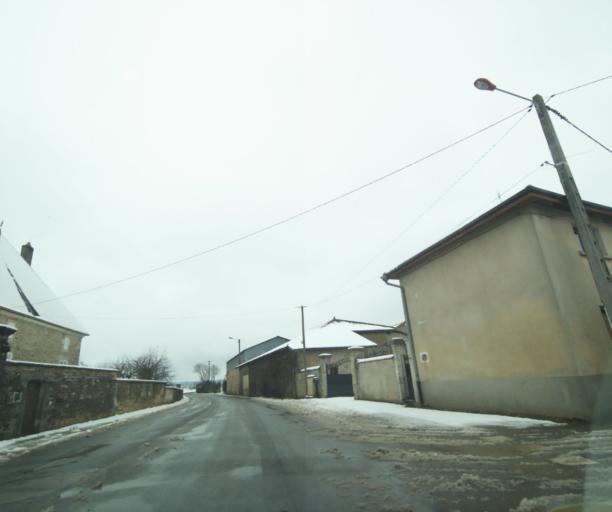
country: FR
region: Champagne-Ardenne
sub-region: Departement de la Haute-Marne
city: Montier-en-Der
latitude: 48.4192
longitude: 4.8208
